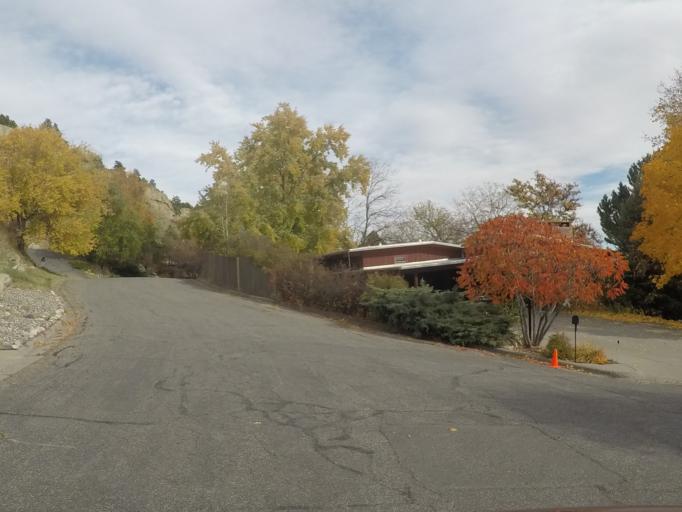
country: US
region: Montana
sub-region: Yellowstone County
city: Billings
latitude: 45.8010
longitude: -108.5500
